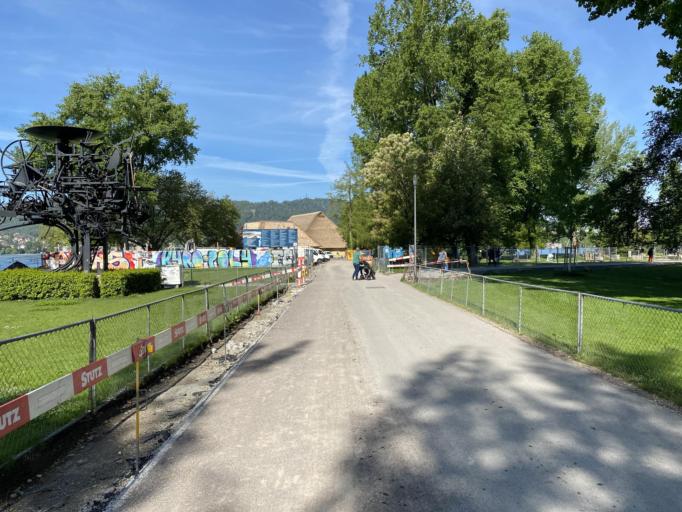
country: CH
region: Zurich
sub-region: Bezirk Zuerich
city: Zuerich (Kreis 8) / Seefeld
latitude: 47.3531
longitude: 8.5526
